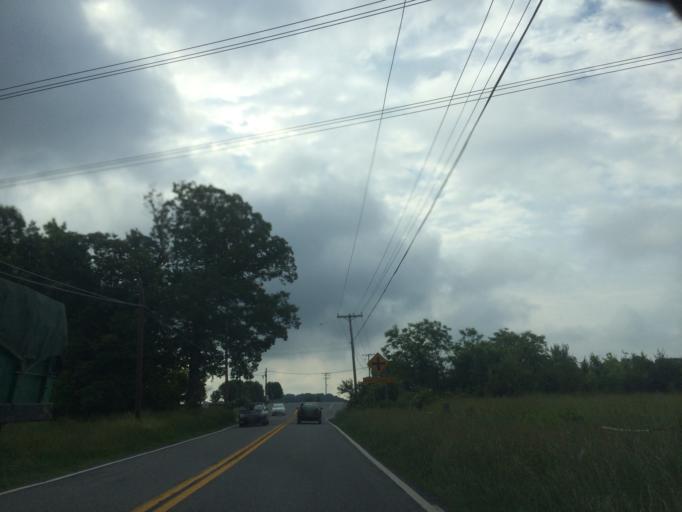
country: US
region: Maryland
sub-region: Montgomery County
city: Olney
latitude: 39.2106
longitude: -77.0411
